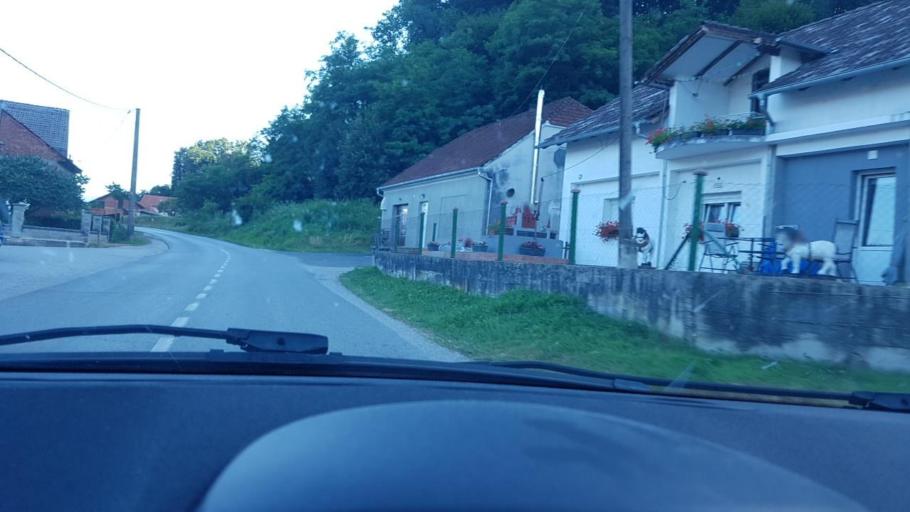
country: HR
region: Krapinsko-Zagorska
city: Bedekovcina
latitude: 46.0625
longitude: 16.0038
